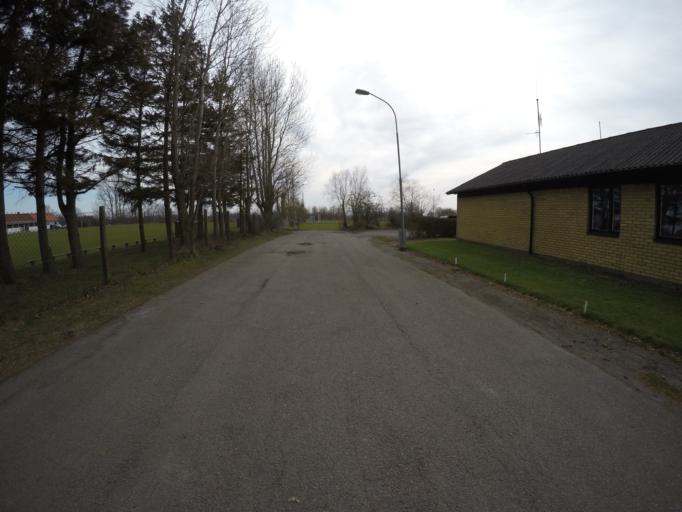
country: SE
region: Skane
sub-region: Ystads Kommun
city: Kopingebro
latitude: 55.4375
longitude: 14.1081
